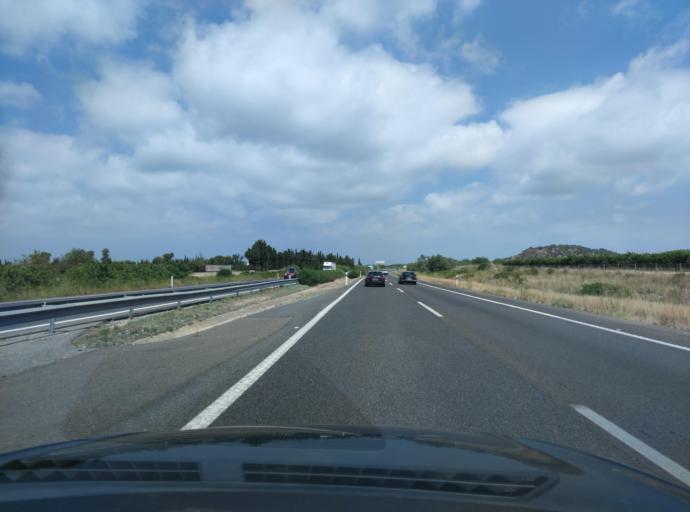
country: ES
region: Valencia
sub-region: Provincia de Castello
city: Vinaros
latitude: 40.4828
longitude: 0.4175
